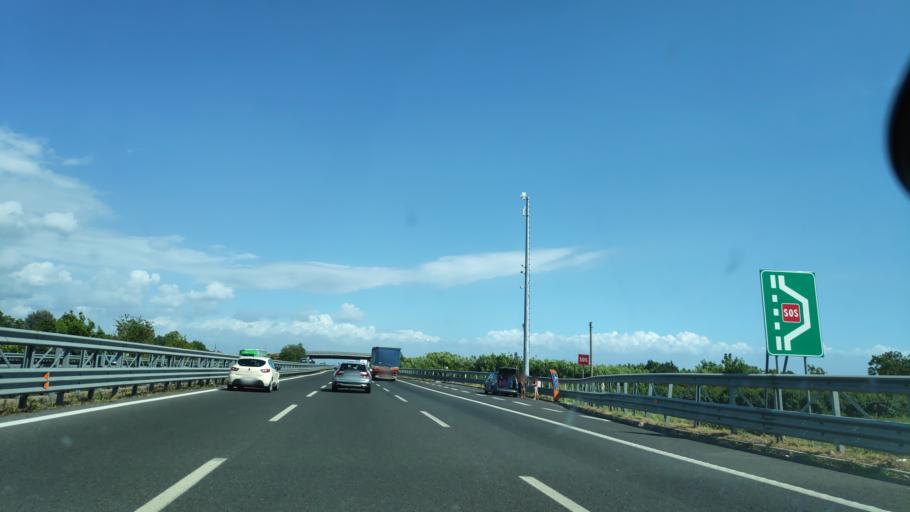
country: IT
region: Campania
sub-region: Provincia di Salerno
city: Pontecagnano
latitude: 40.6480
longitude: 14.8837
